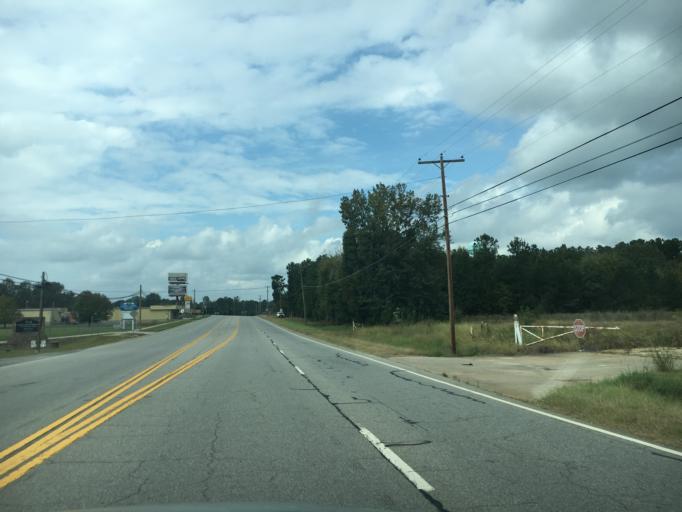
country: US
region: Georgia
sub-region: Elbert County
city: Elberton
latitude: 34.0843
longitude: -82.8447
